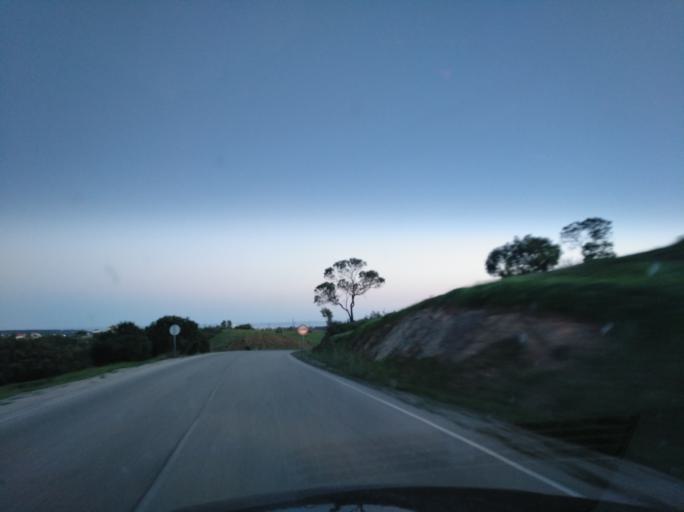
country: PT
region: Faro
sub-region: Vila Real de Santo Antonio
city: Monte Gordo
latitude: 37.2082
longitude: -7.5196
